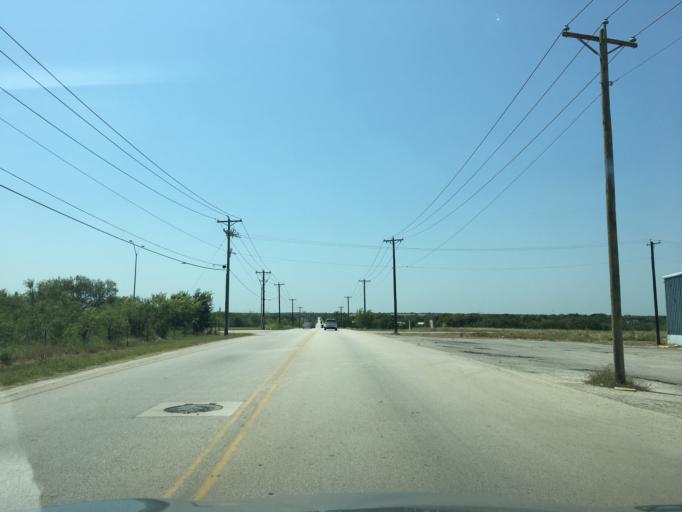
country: US
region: Texas
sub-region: Tarrant County
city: Edgecliff Village
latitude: 32.6141
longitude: -97.3357
